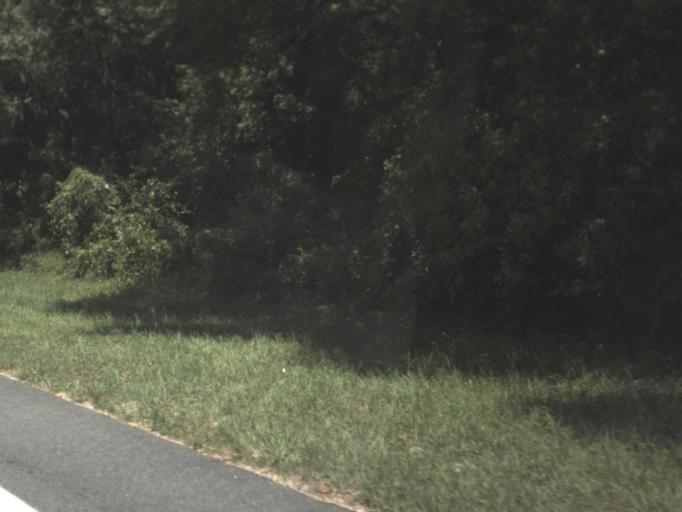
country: US
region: Florida
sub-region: Dixie County
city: Cross City
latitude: 29.7927
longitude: -82.9731
